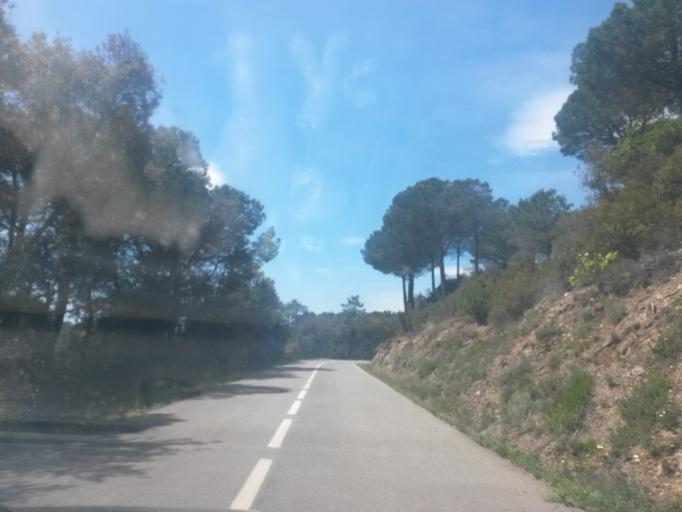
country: ES
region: Catalonia
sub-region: Provincia de Girona
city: Cassa de la Selva
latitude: 41.9188
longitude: 2.9143
